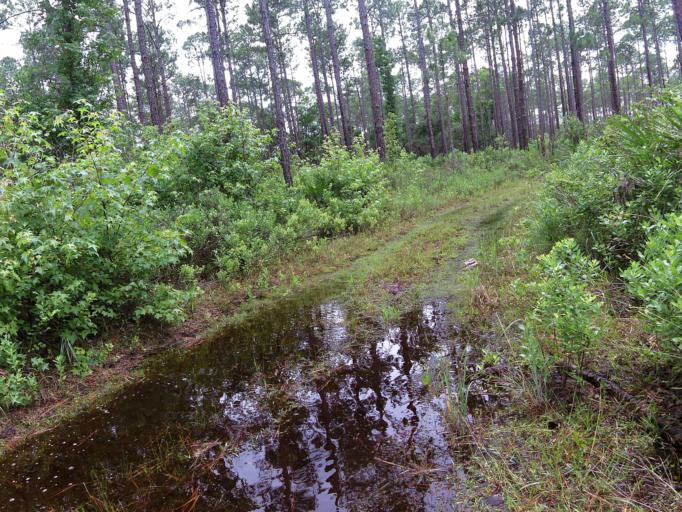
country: US
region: Florida
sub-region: Clay County
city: Green Cove Springs
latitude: 29.9648
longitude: -81.6283
